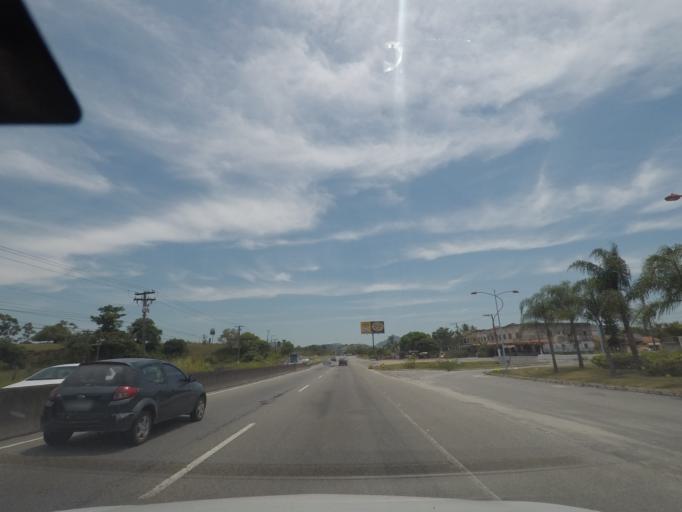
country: BR
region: Rio de Janeiro
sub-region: Marica
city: Marica
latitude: -22.9162
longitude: -42.8495
